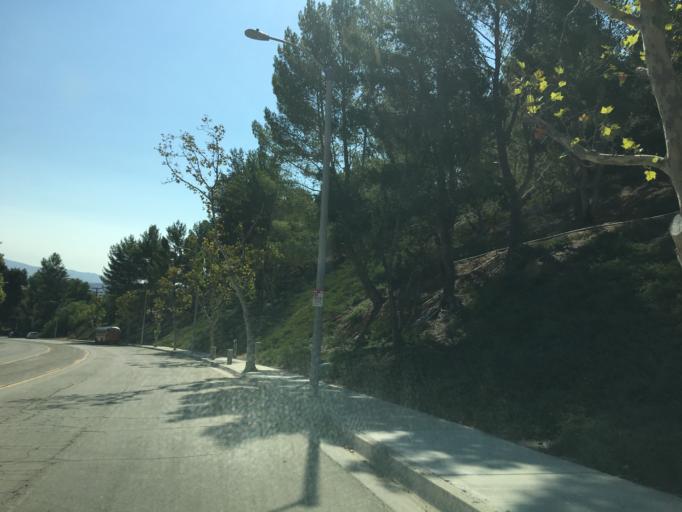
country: US
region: California
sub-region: Los Angeles County
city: Castaic
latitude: 34.4889
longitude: -118.6315
